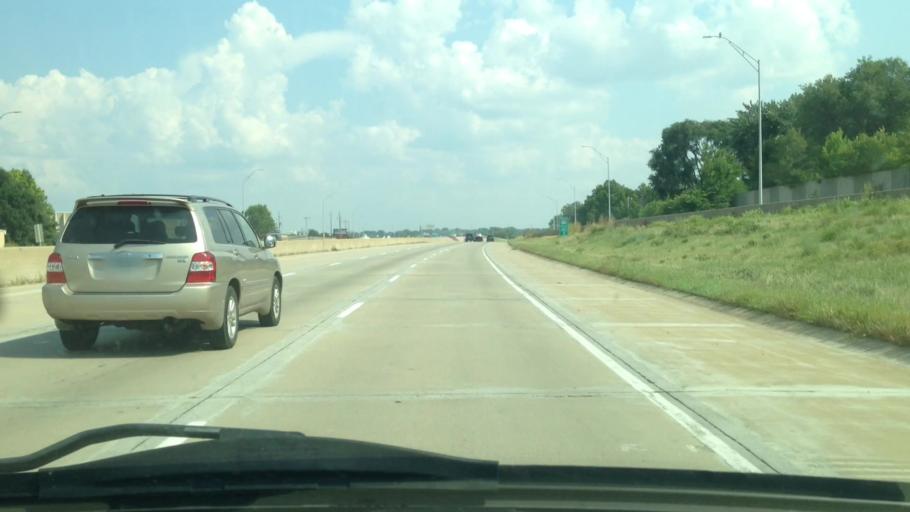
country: US
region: Iowa
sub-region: Black Hawk County
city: Waterloo
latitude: 42.5070
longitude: -92.3731
